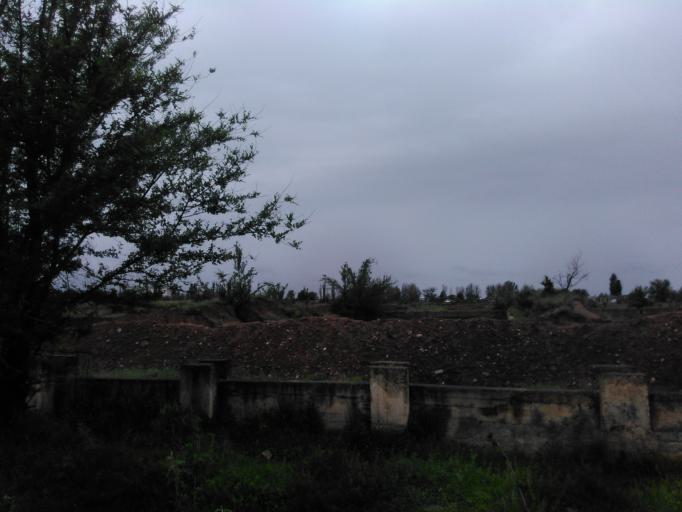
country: KG
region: Chuy
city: Tokmok
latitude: 42.8129
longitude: 75.3304
